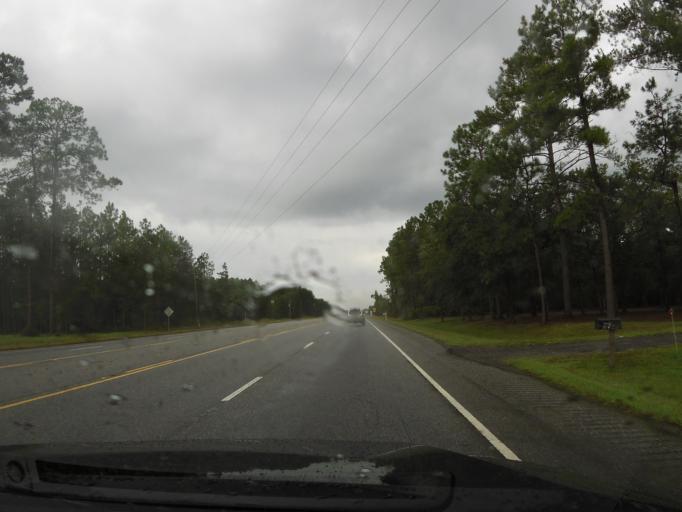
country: US
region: Georgia
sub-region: Wayne County
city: Jesup
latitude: 31.5757
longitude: -81.8472
